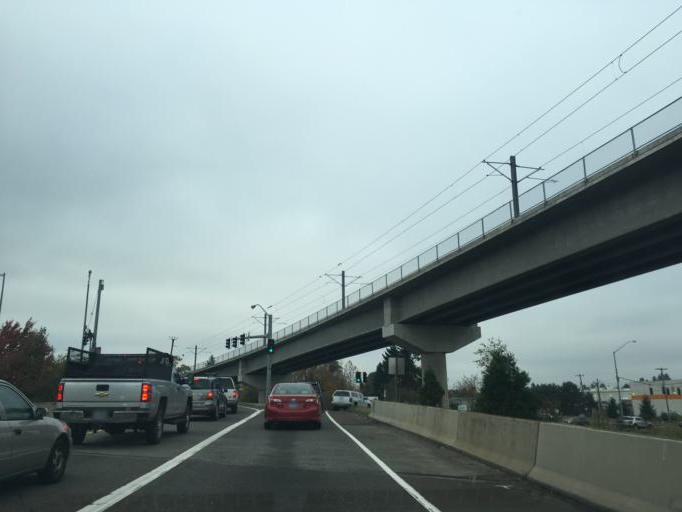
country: US
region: Oregon
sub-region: Multnomah County
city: Lents
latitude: 45.4575
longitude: -122.5737
